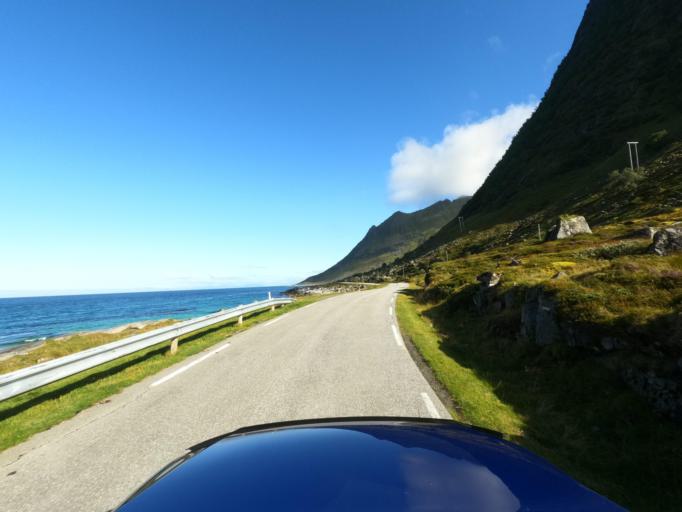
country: NO
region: Nordland
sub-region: Vagan
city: Kabelvag
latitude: 68.3199
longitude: 14.3099
